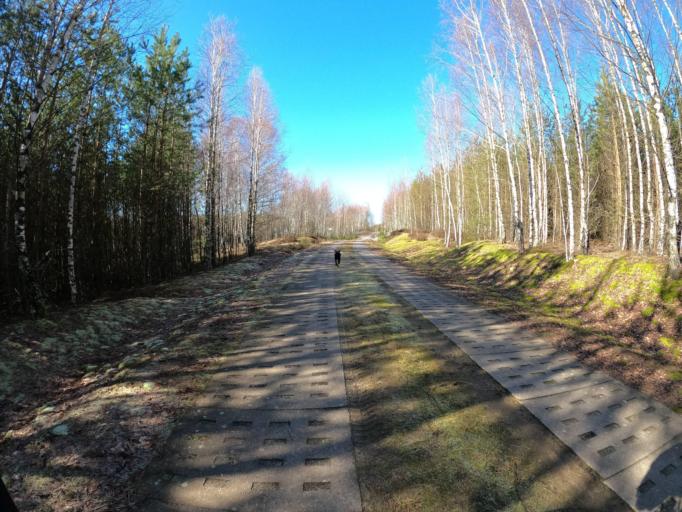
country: PL
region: Greater Poland Voivodeship
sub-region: Powiat zlotowski
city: Sypniewo
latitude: 53.5354
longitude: 16.5986
